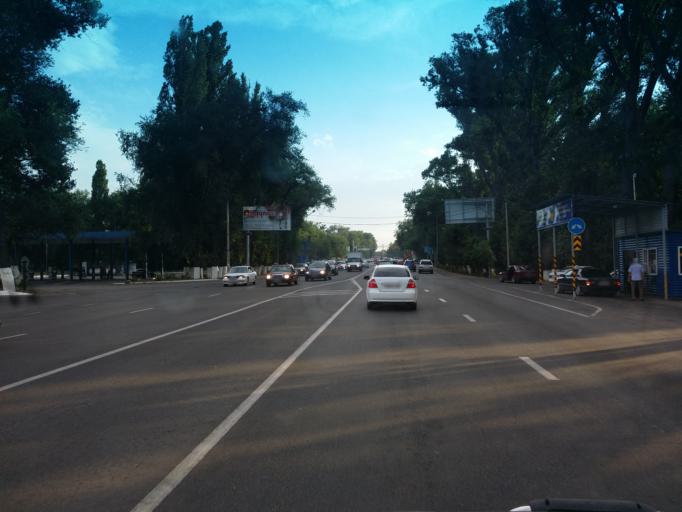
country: KZ
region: Almaty Qalasy
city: Almaty
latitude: 43.2974
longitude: 77.0004
